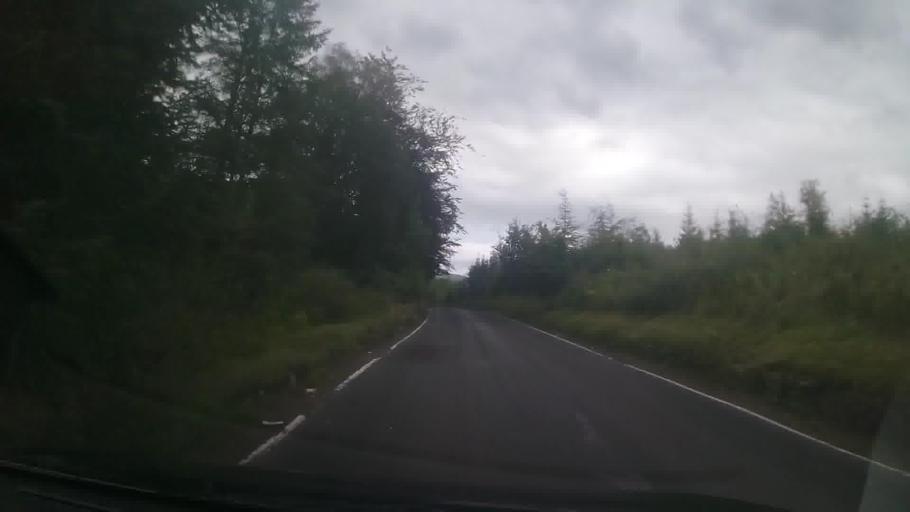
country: GB
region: Scotland
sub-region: Argyll and Bute
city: Garelochhead
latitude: 56.2412
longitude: -5.0866
